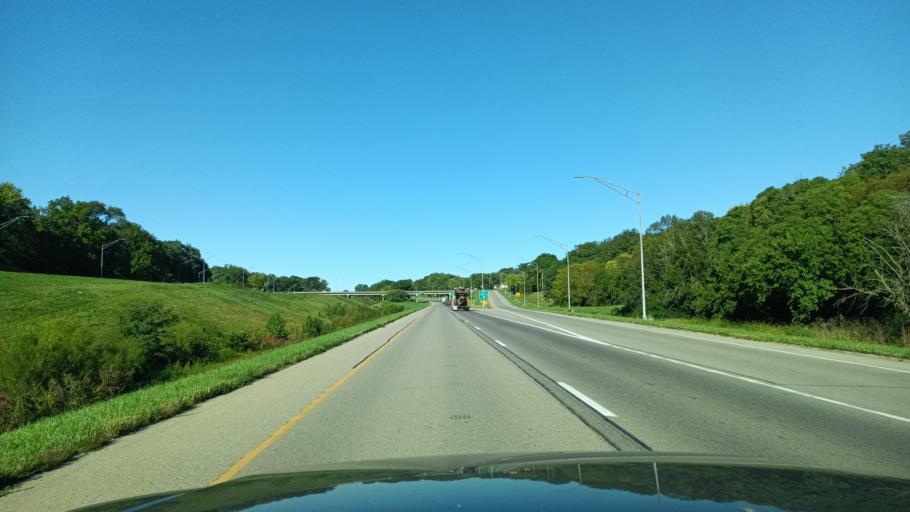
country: US
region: Iowa
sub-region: Des Moines County
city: Burlington
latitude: 40.8172
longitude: -91.1204
